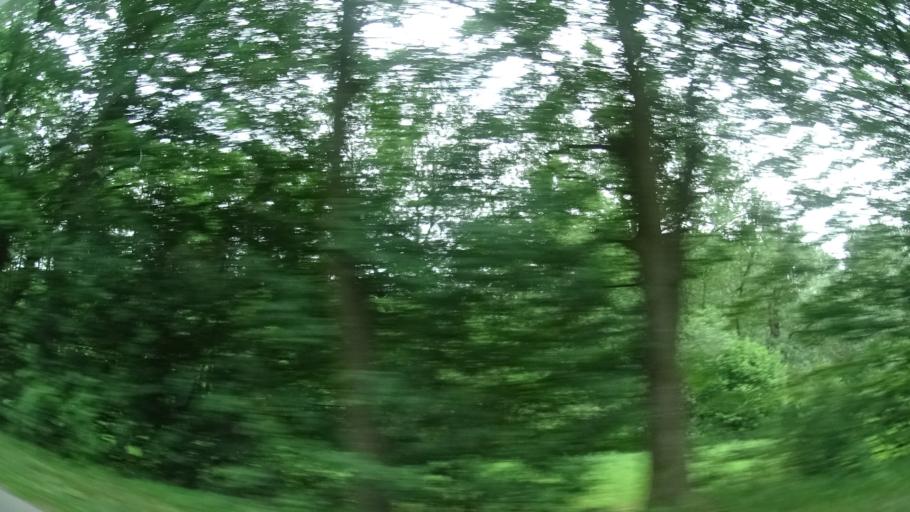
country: DE
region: North Rhine-Westphalia
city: Brakel
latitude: 51.6518
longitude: 9.1430
